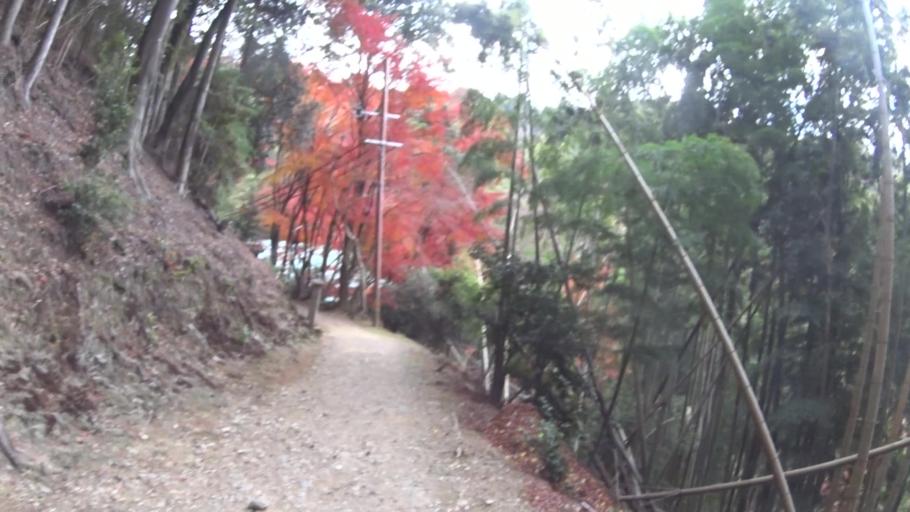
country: JP
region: Kyoto
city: Uji
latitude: 34.9432
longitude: 135.8375
